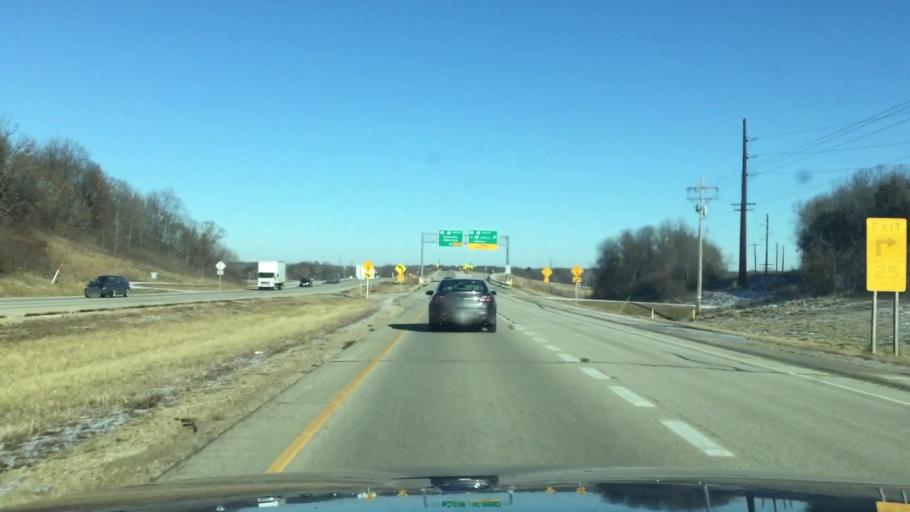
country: US
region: Wisconsin
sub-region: Racine County
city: Browns Lake
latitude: 42.7135
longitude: -88.2316
